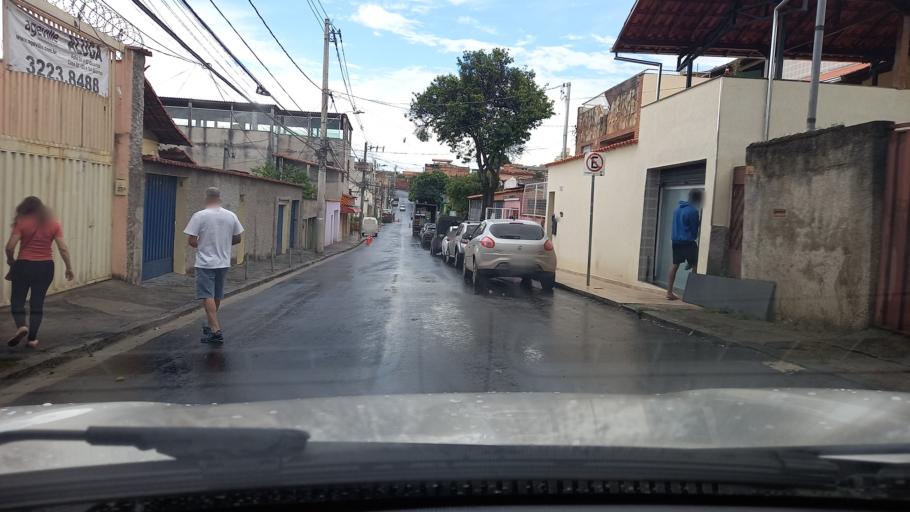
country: BR
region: Minas Gerais
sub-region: Belo Horizonte
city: Belo Horizonte
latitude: -19.9040
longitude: -43.9532
